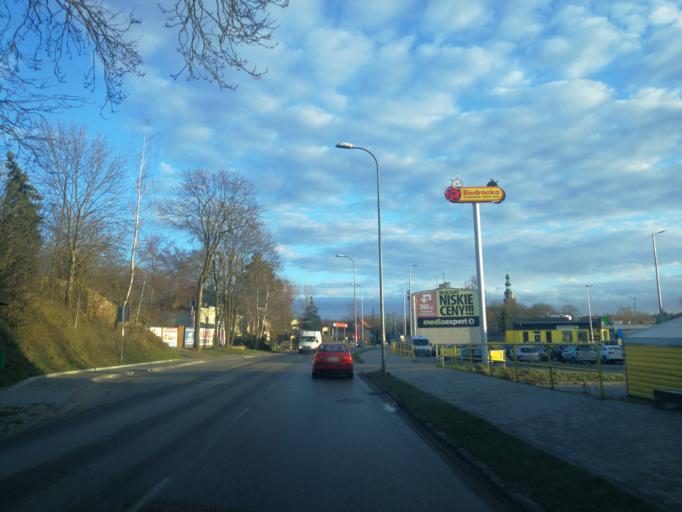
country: PL
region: Kujawsko-Pomorskie
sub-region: Powiat torunski
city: Chelmza
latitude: 53.1921
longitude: 18.6132
